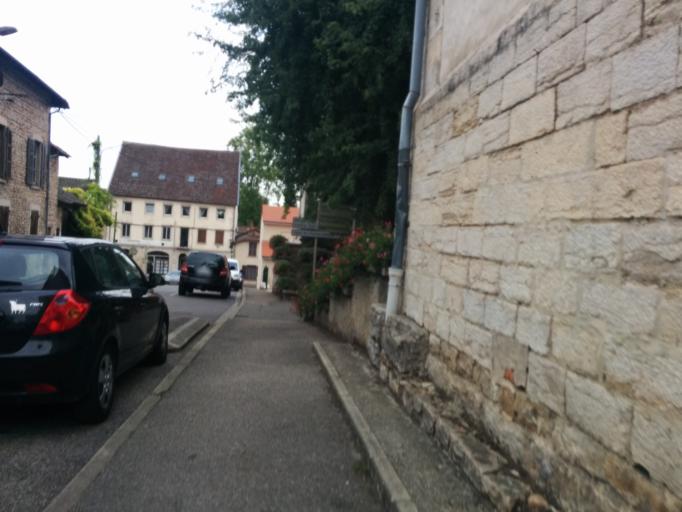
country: FR
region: Rhone-Alpes
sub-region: Departement de l'Ain
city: Meximieux
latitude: 45.9052
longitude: 5.1962
